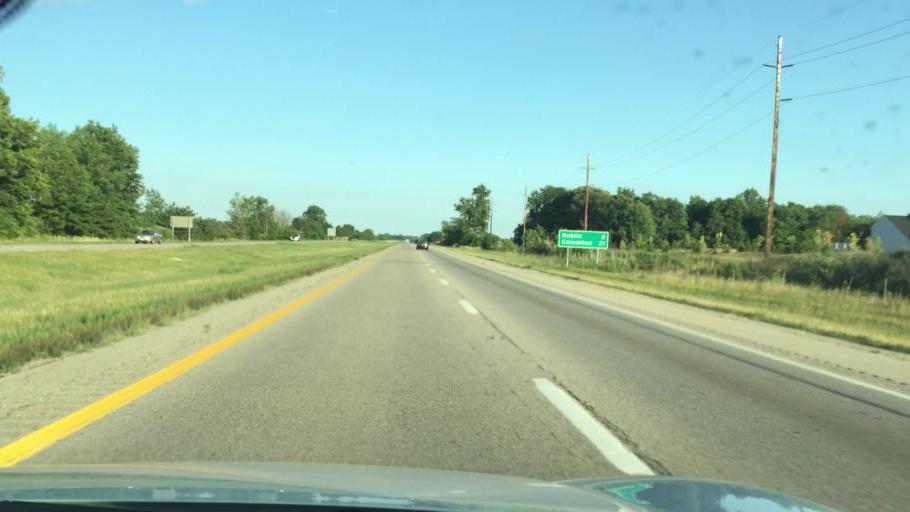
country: US
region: Ohio
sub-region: Union County
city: New California
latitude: 40.1517
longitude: -83.2199
